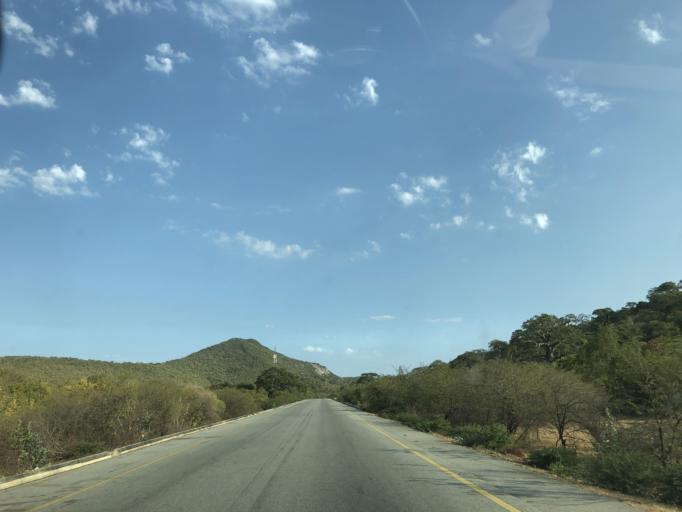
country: AO
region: Benguela
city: Benguela
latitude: -13.2675
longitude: 13.7937
